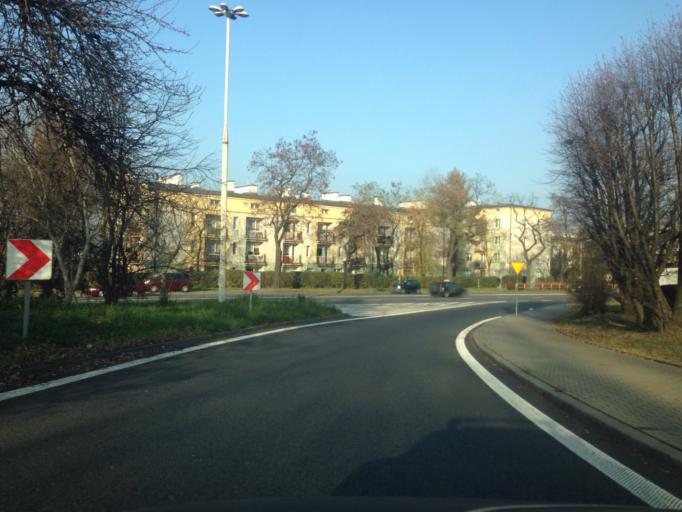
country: PL
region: Silesian Voivodeship
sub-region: Katowice
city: Katowice
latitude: 50.2504
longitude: 19.0027
